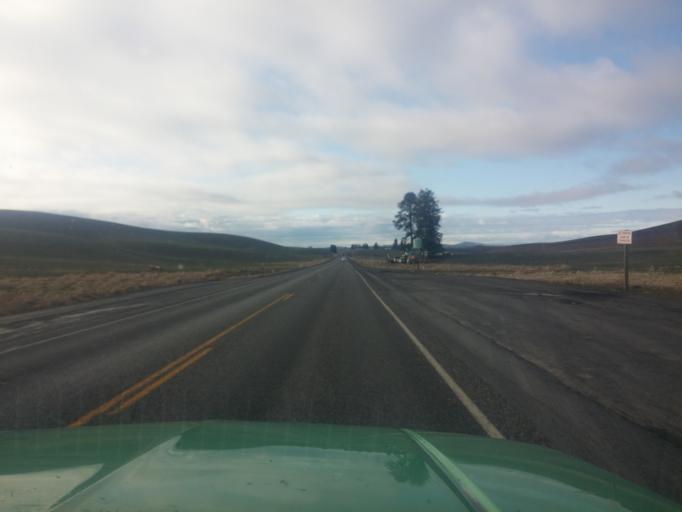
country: US
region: Idaho
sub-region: Latah County
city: Moscow
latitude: 46.7927
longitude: -116.9957
